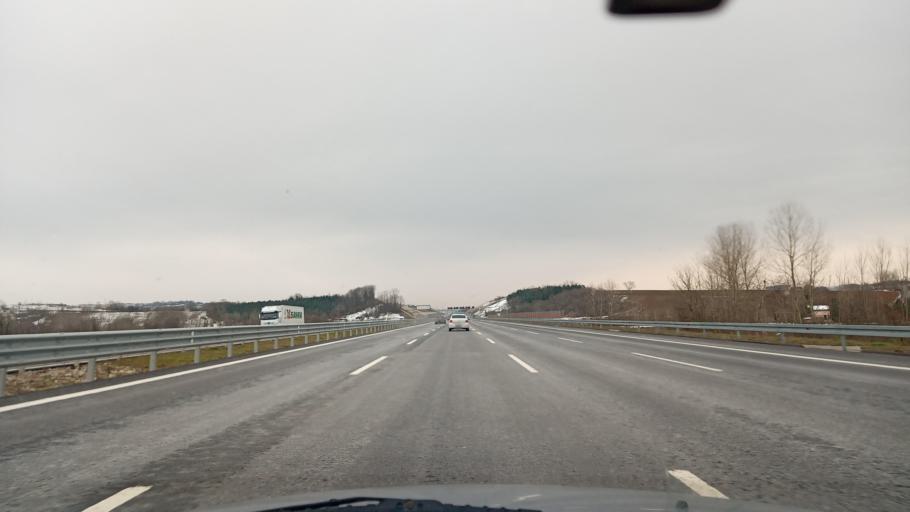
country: TR
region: Kocaeli
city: Akmese
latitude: 40.8466
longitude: 30.2447
